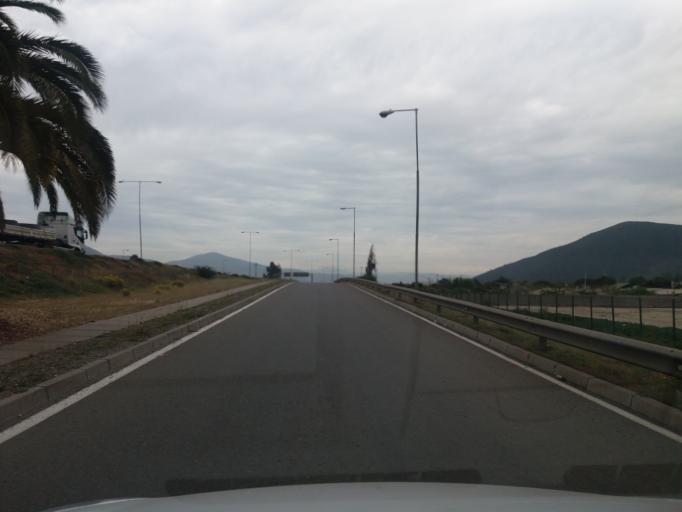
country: CL
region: Valparaiso
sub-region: Provincia de Quillota
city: Hacienda La Calera
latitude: -32.8416
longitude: -71.1091
